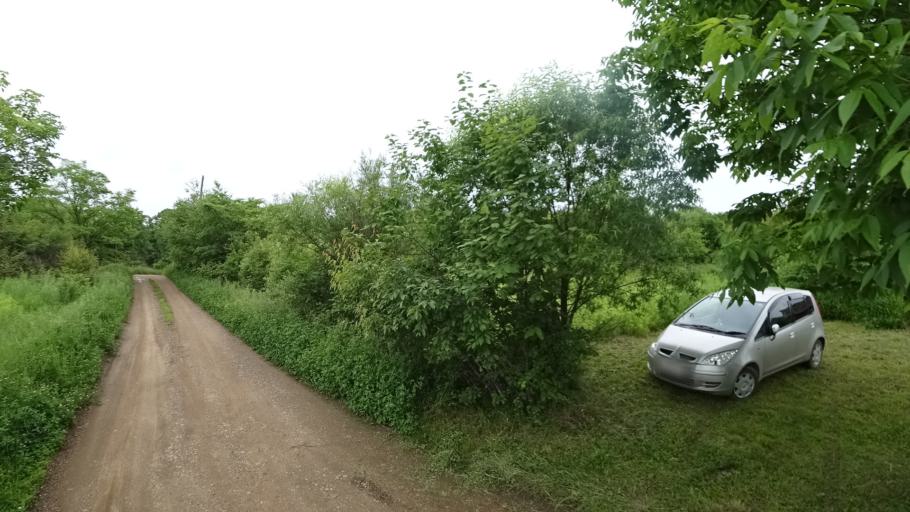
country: RU
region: Primorskiy
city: Novosysoyevka
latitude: 44.2101
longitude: 133.3275
